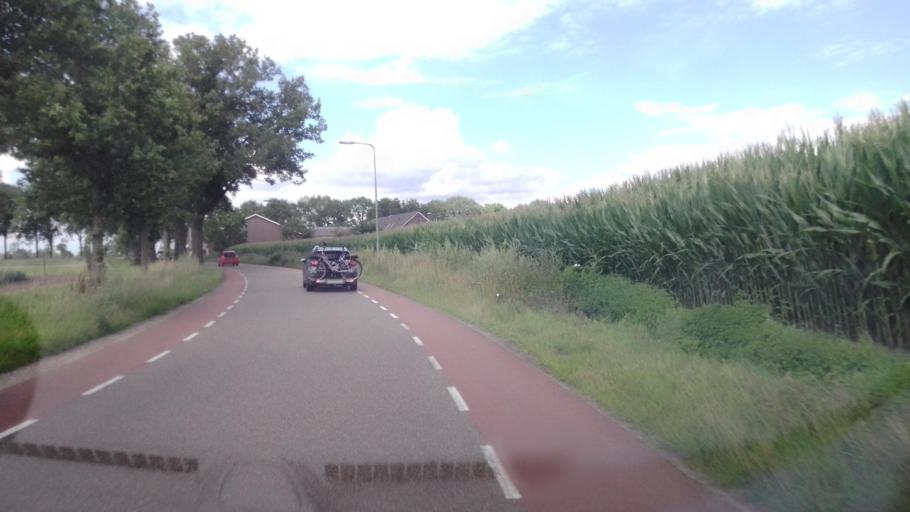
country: NL
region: Limburg
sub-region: Gemeente Peel en Maas
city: Maasbree
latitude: 51.3544
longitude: 6.0310
